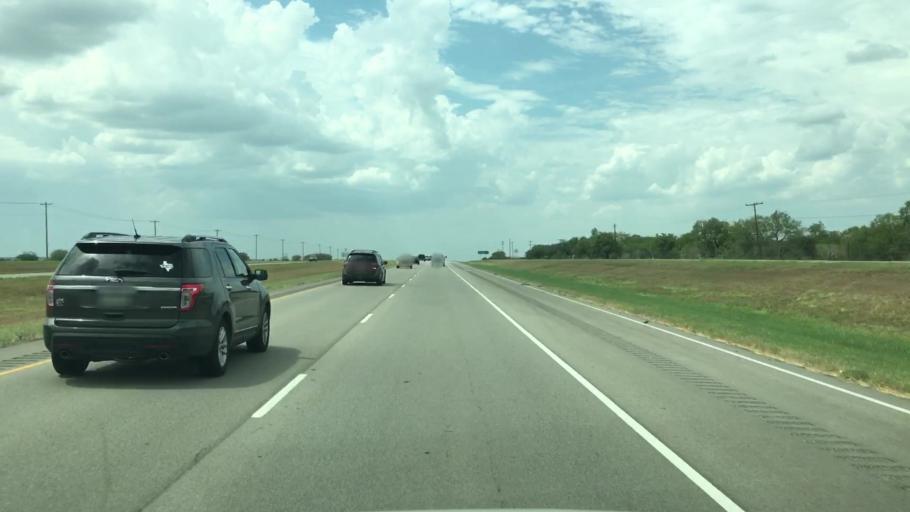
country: US
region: Texas
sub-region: Live Oak County
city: Three Rivers
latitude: 28.4986
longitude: -98.1534
